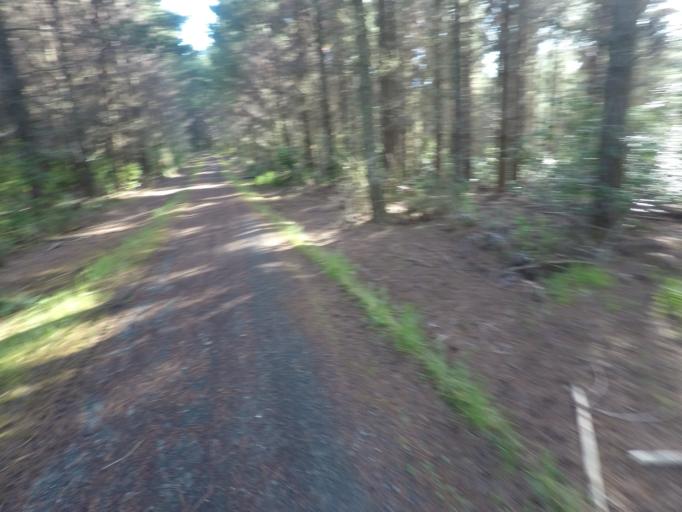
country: NZ
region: Auckland
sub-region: Auckland
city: Parakai
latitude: -36.7098
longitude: 174.5782
